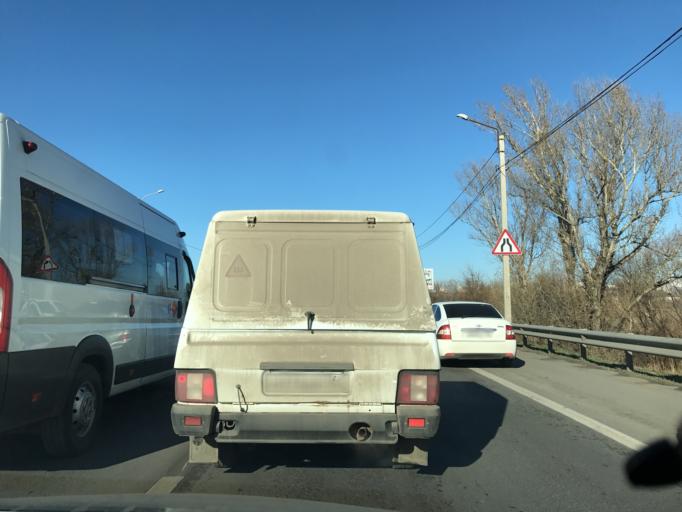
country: RU
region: Rostov
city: Rostov-na-Donu
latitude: 47.1945
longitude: 39.7325
